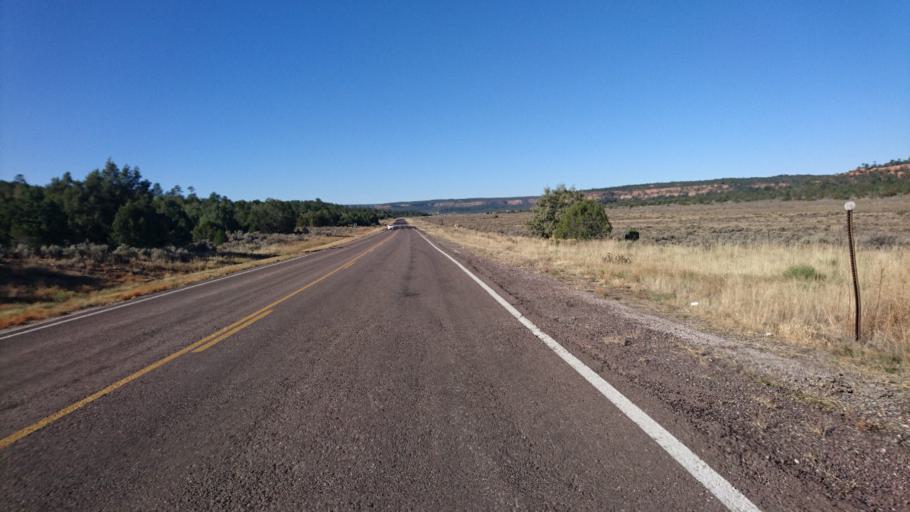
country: US
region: New Mexico
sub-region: McKinley County
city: Black Rock
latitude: 35.1197
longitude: -108.5454
